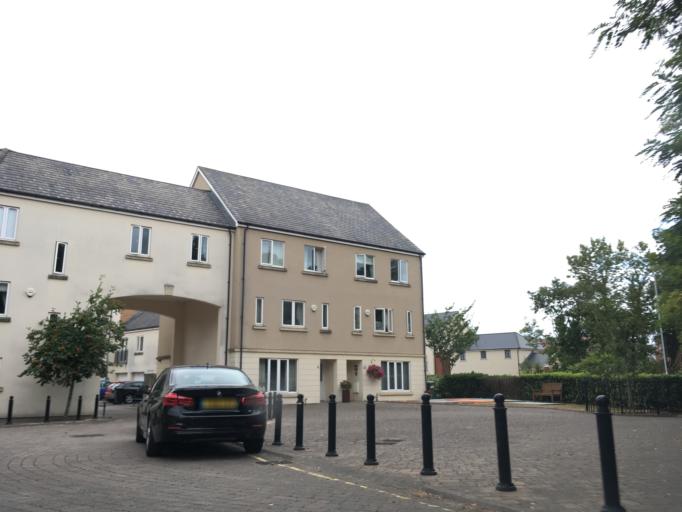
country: GB
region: England
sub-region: South Gloucestershire
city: Stoke Gifford
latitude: 51.4952
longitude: -2.5430
